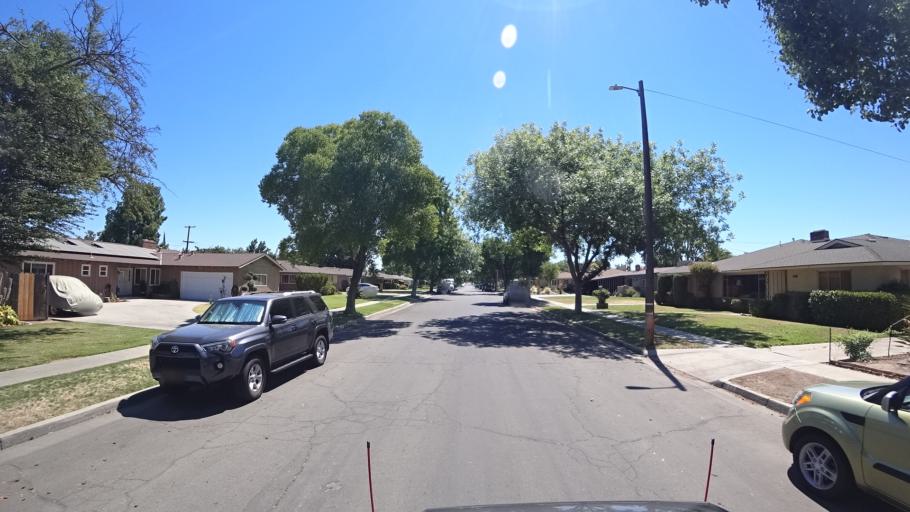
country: US
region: California
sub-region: Fresno County
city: Fresno
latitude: 36.7821
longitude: -119.8148
